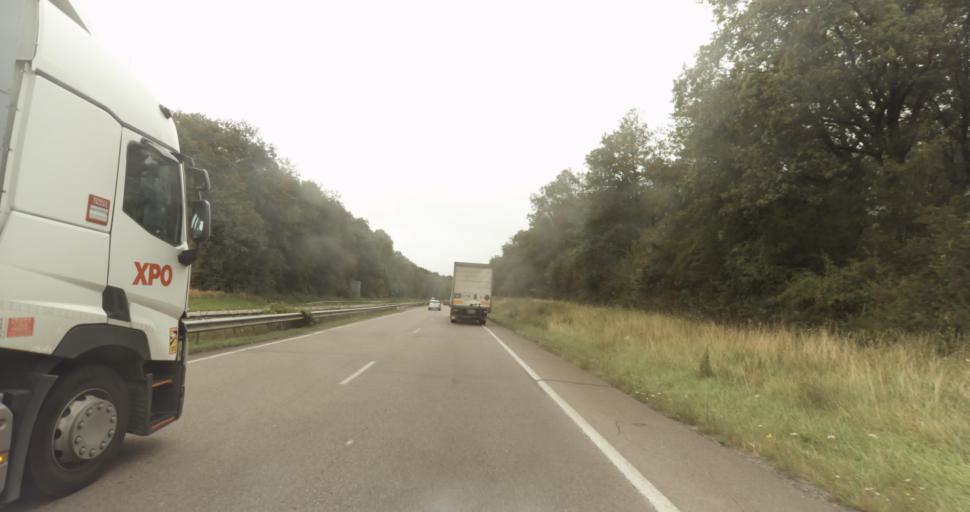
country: FR
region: Haute-Normandie
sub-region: Departement de l'Eure
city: Heudreville-sur-Eure
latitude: 49.1048
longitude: 1.1884
